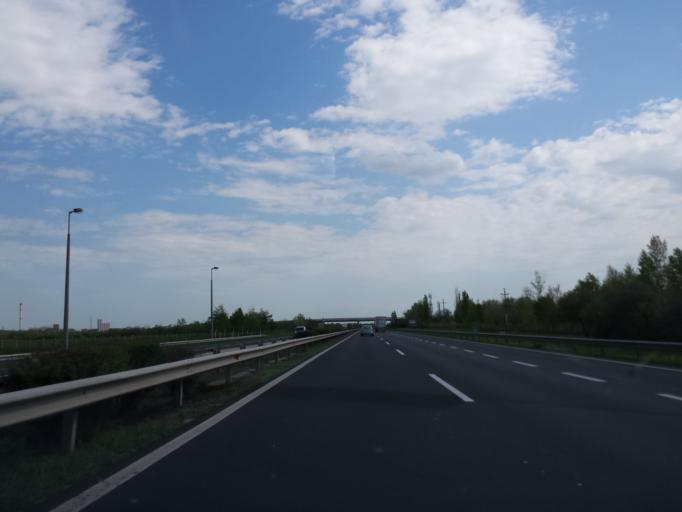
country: HU
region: Gyor-Moson-Sopron
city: Mosonmagyarovar
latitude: 47.8695
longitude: 17.2201
